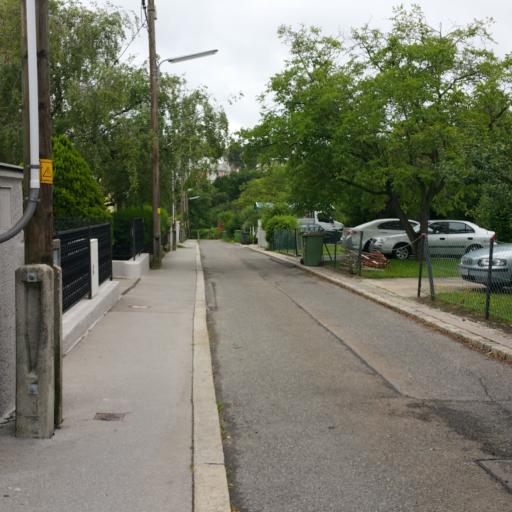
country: AT
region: Vienna
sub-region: Wien Stadt
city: Vienna
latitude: 48.2134
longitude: 16.2881
